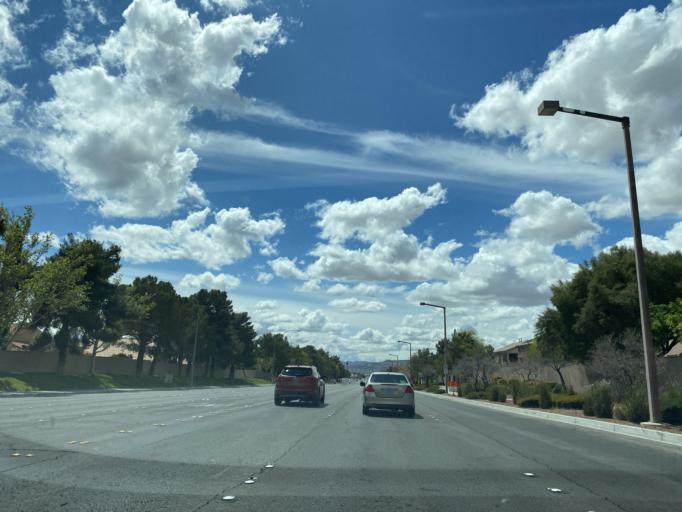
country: US
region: Nevada
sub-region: Clark County
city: Summerlin South
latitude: 36.1371
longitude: -115.3154
